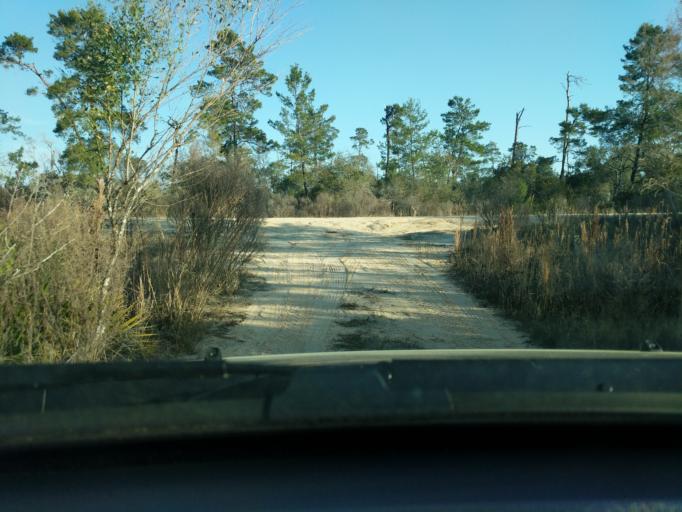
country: US
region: Florida
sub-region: Lake County
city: Astor
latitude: 29.2257
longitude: -81.7410
